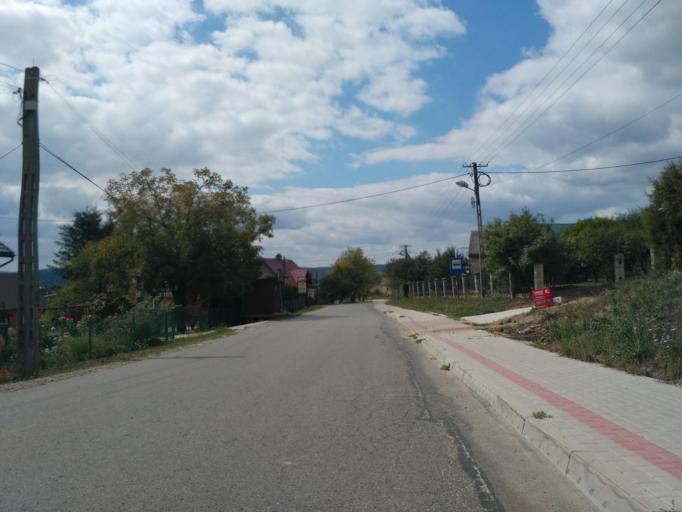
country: PL
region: Subcarpathian Voivodeship
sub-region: Powiat rzeszowski
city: Dynow
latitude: 49.8136
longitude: 22.2663
